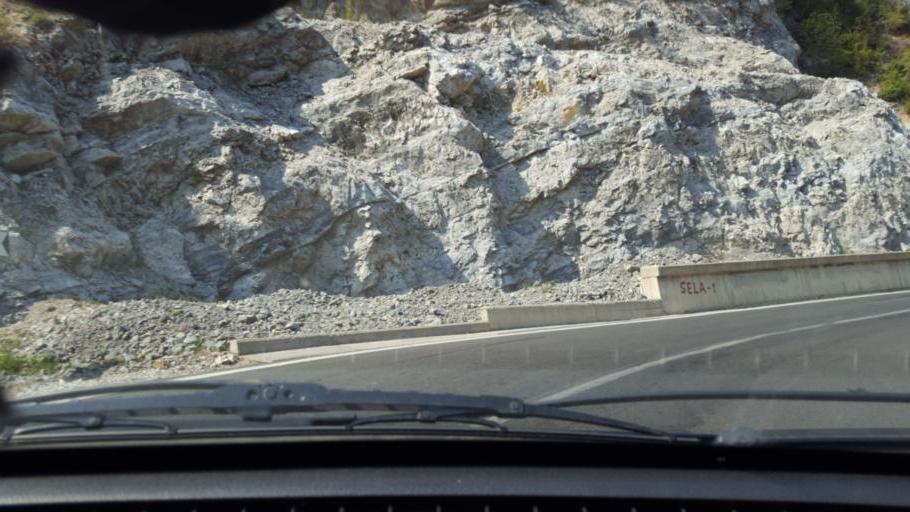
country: AL
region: Shkoder
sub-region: Rrethi i Malesia e Madhe
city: Kastrat
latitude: 42.4123
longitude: 19.5100
